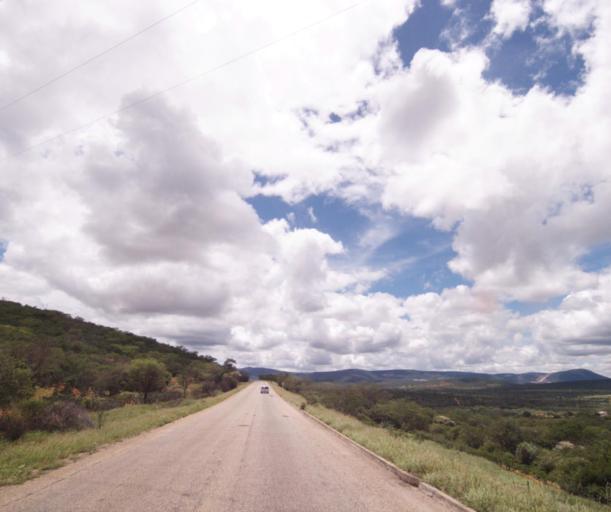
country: BR
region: Bahia
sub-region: Brumado
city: Brumado
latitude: -14.1993
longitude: -41.6107
